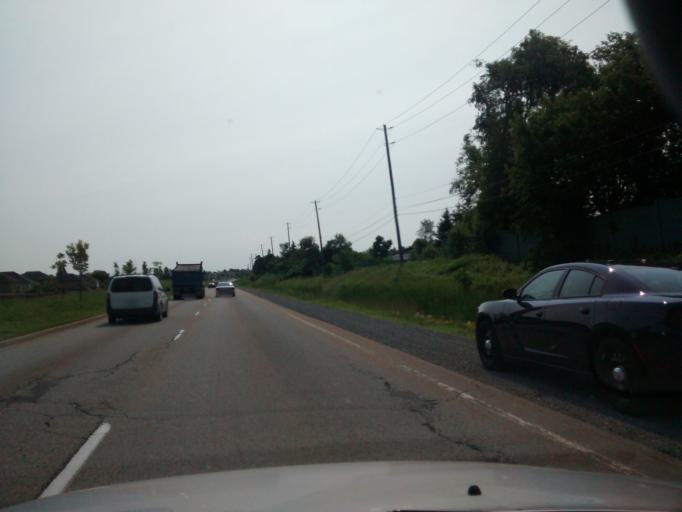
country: CA
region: Ontario
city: Hamilton
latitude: 43.1964
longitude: -79.8040
